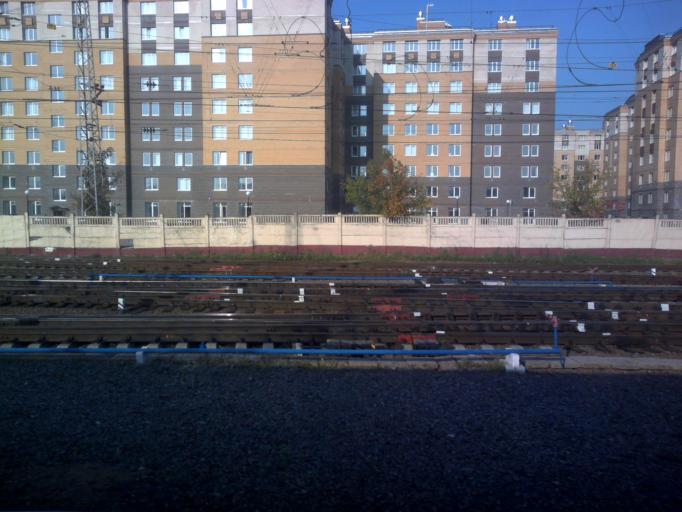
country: RU
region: Leningrad
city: Finlyandskiy
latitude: 59.9608
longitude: 30.3592
